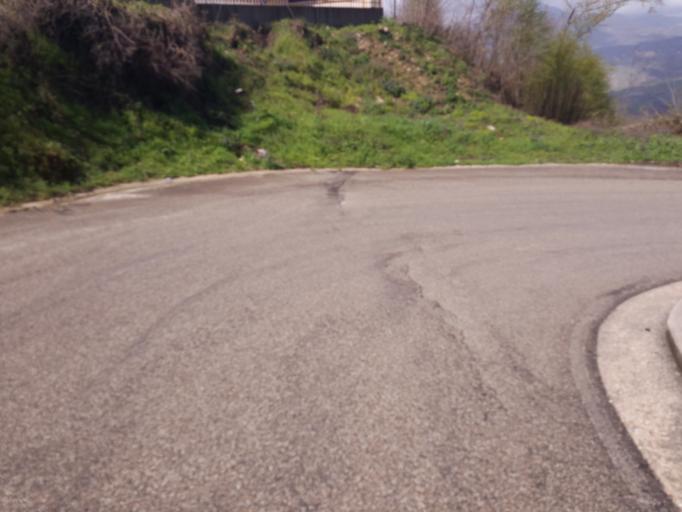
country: IT
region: Campania
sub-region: Provincia di Avellino
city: Roccabascerana
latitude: 41.0398
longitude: 14.7135
